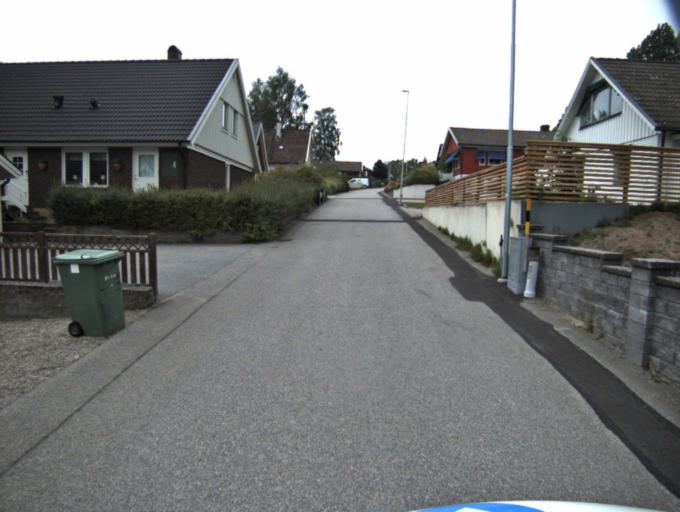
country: SE
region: Vaestra Goetaland
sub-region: Ulricehamns Kommun
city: Ulricehamn
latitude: 57.8460
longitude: 13.2761
